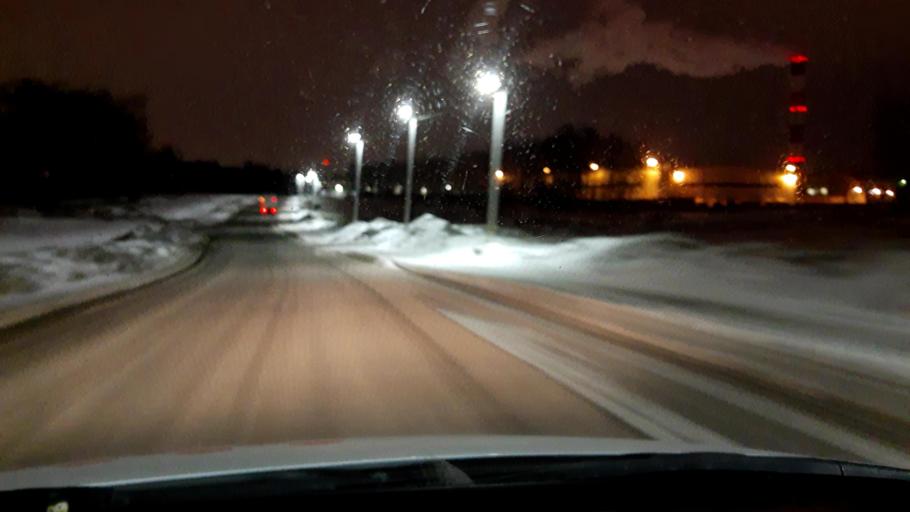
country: RU
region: Moskovskaya
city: Kommunarka
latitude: 55.5526
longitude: 37.5145
